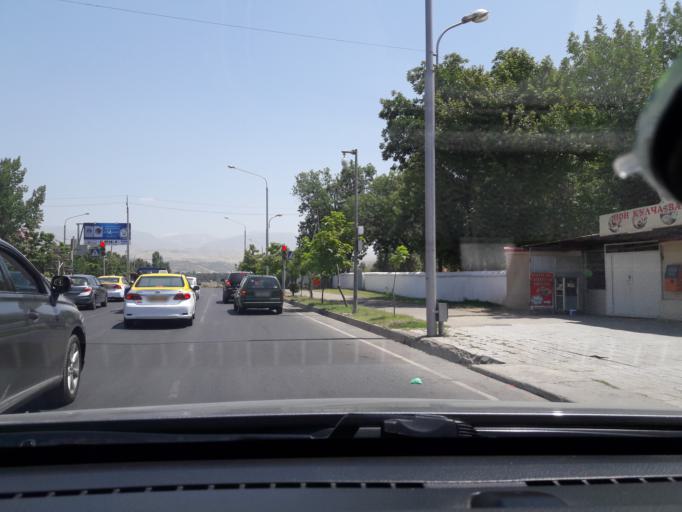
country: TJ
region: Dushanbe
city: Dushanbe
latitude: 38.5944
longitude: 68.7539
